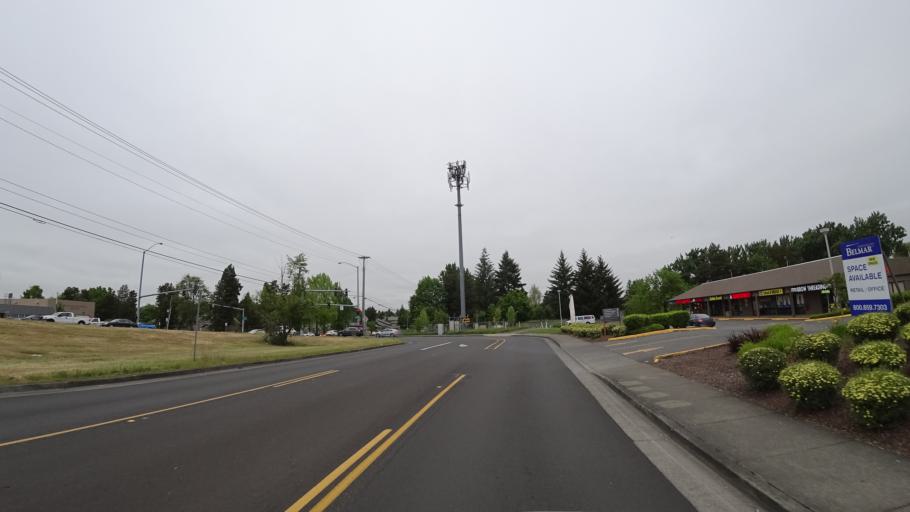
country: US
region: Oregon
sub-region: Washington County
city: Rockcreek
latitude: 45.5429
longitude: -122.8669
